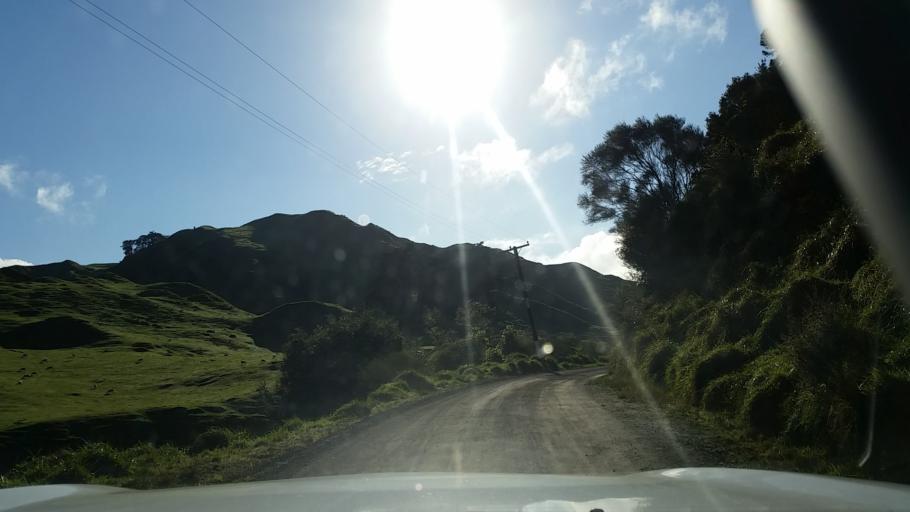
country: NZ
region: Taranaki
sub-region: South Taranaki District
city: Eltham
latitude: -39.5071
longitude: 174.3974
